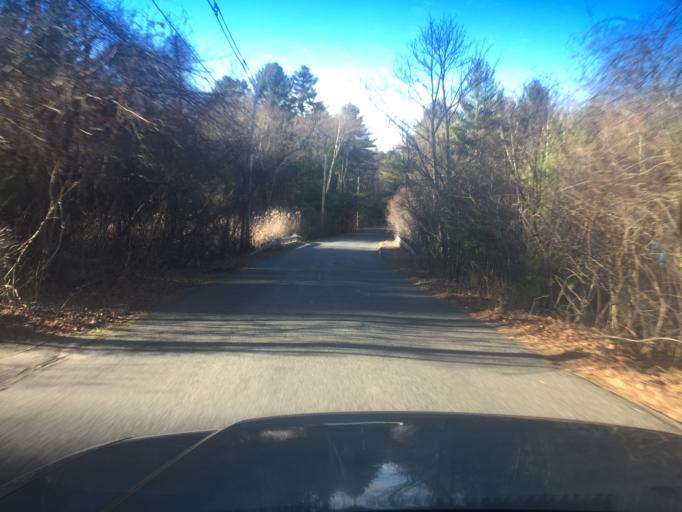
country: US
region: Massachusetts
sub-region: Middlesex County
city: Ashland
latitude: 42.2253
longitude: -71.4763
